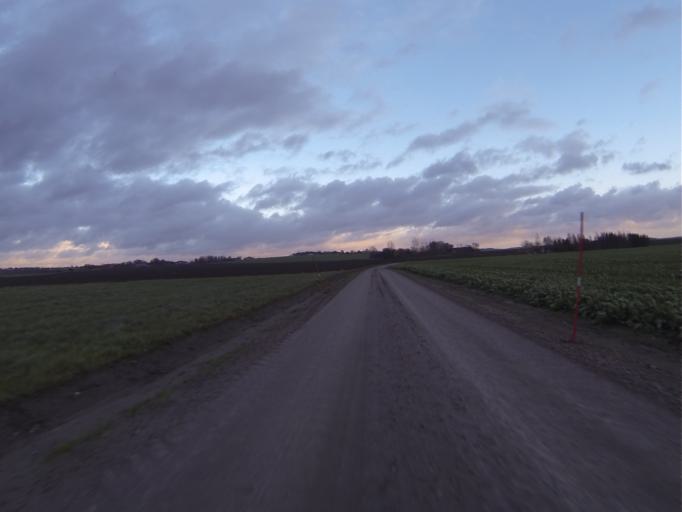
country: SE
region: Skane
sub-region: Lunds Kommun
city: Genarp
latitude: 55.6420
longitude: 13.3315
